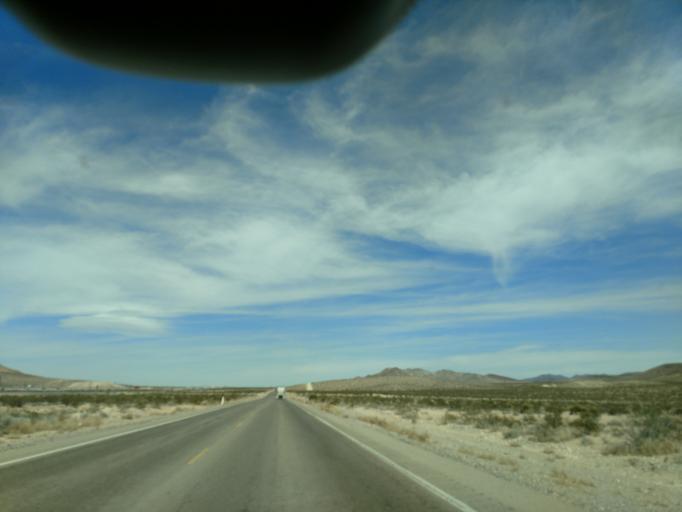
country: US
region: Nevada
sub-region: Clark County
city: Enterprise
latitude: 35.8582
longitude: -115.2526
